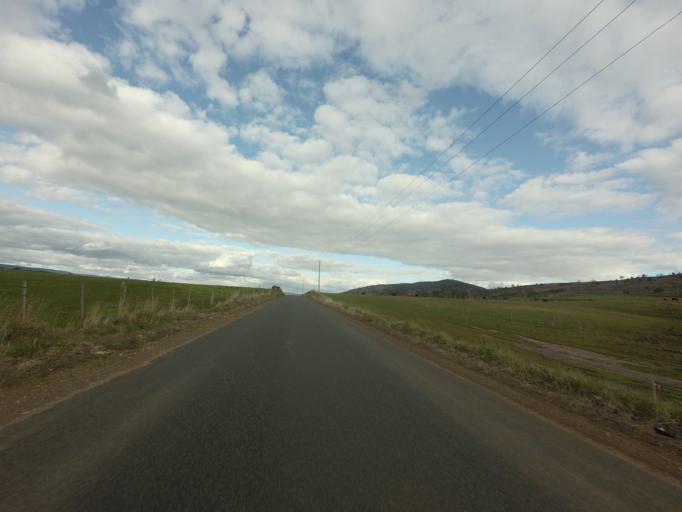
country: AU
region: Tasmania
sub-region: Northern Midlands
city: Evandale
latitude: -41.9105
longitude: 147.3718
